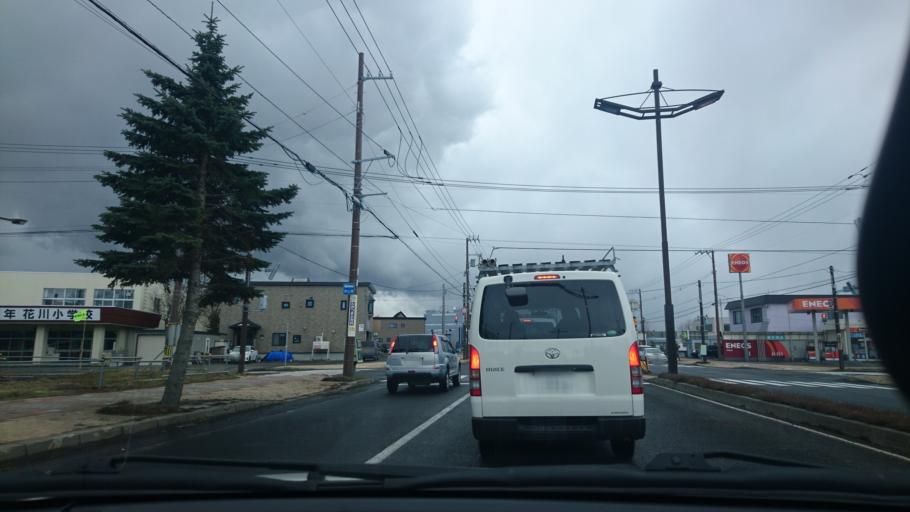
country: JP
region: Hokkaido
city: Ishikari
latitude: 43.1748
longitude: 141.3167
